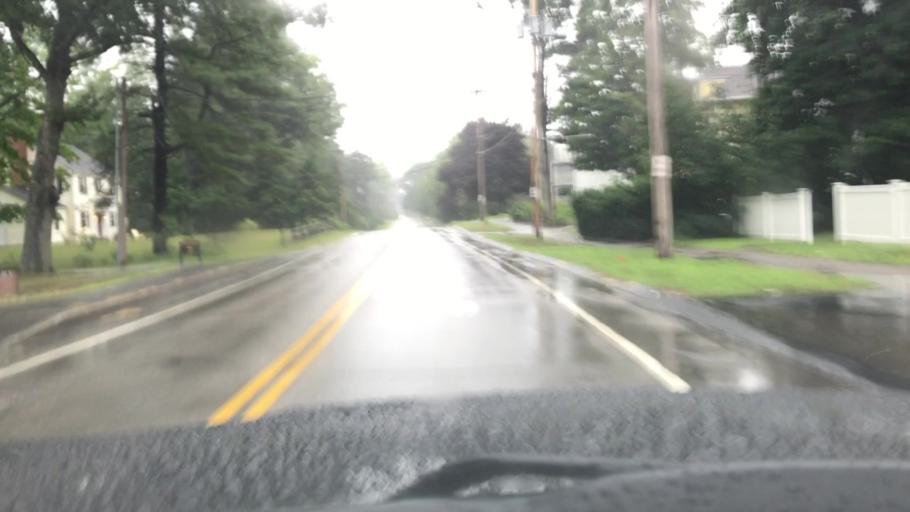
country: US
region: New Hampshire
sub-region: Strafford County
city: Durham
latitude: 43.1398
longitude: -70.9262
